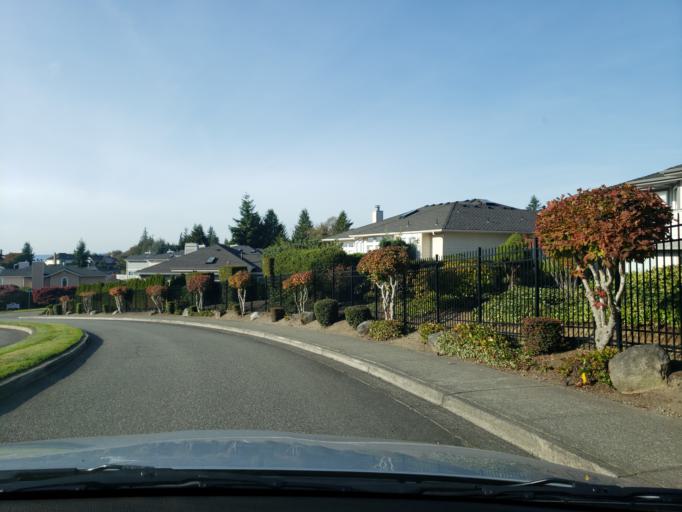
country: US
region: Washington
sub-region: Snohomish County
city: Meadowdale
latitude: 47.8725
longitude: -122.3187
